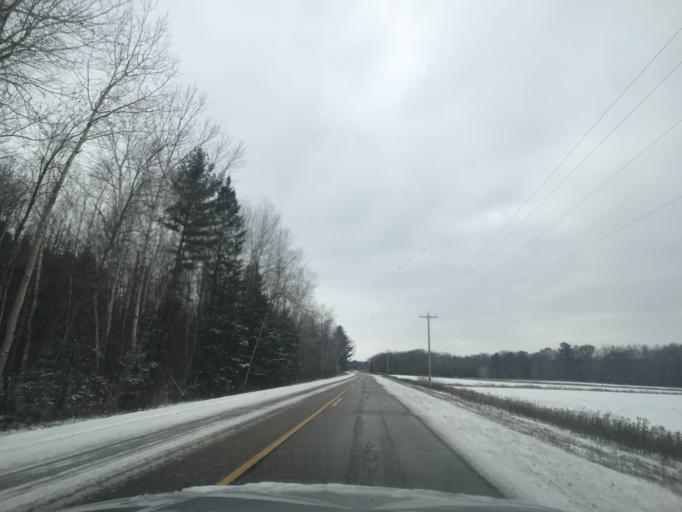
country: US
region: Wisconsin
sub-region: Brown County
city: Suamico
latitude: 44.7063
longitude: -88.0726
